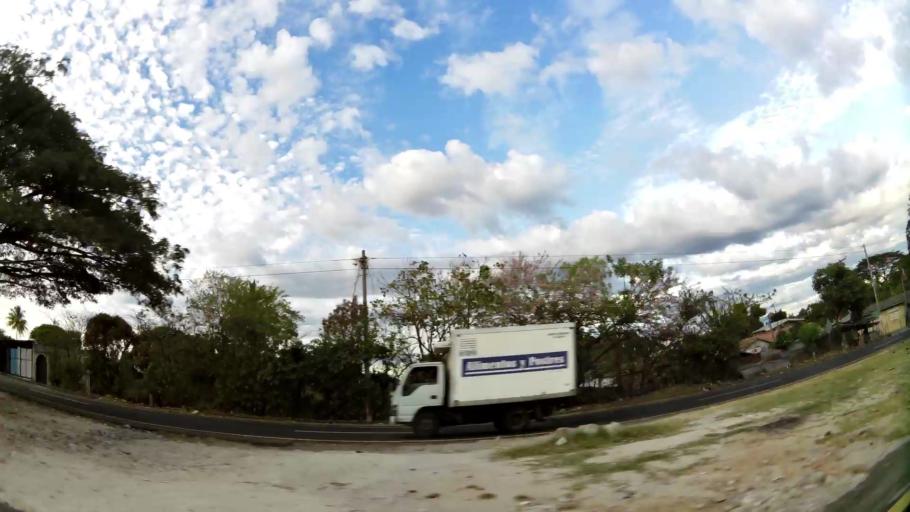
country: SV
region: Cuscatlan
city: Cojutepeque
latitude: 13.7292
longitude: -88.8874
